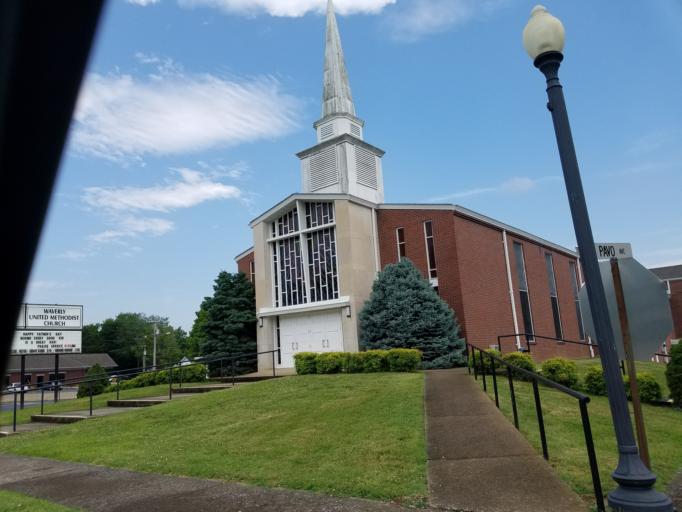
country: US
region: Tennessee
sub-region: Humphreys County
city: Waverly
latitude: 36.0835
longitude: -87.7959
